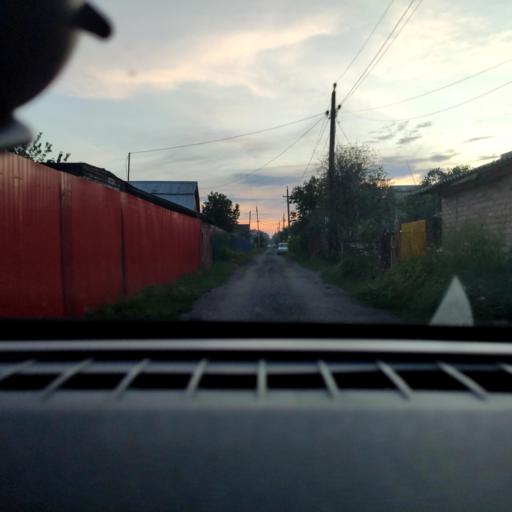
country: RU
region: Samara
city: Tol'yatti
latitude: 53.6314
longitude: 49.4143
